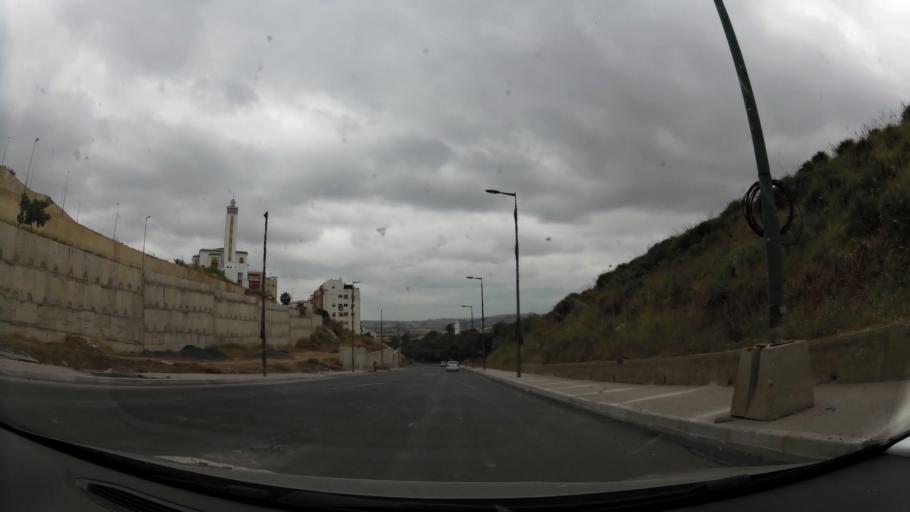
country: MA
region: Rabat-Sale-Zemmour-Zaer
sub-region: Rabat
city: Rabat
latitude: 33.9827
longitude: -6.8065
